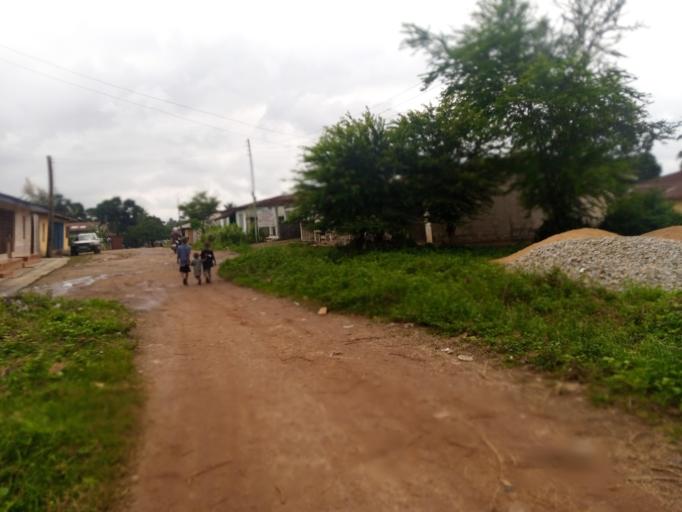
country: SL
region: Eastern Province
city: Kenema
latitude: 7.8622
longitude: -11.1945
